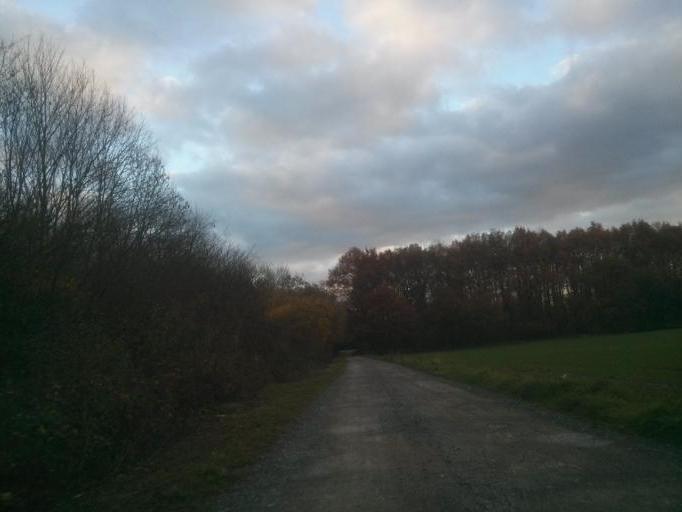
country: DE
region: North Rhine-Westphalia
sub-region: Regierungsbezirk Koln
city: Poll
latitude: 50.9071
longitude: 7.0069
